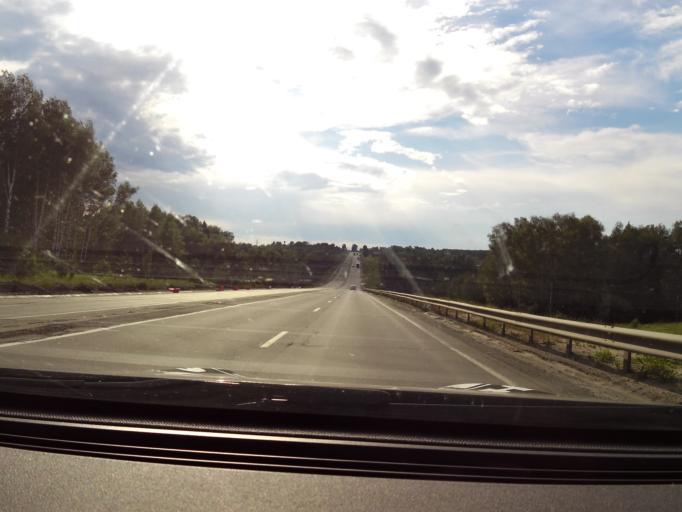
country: RU
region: Vladimir
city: Gorokhovets
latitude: 56.1704
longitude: 42.4354
